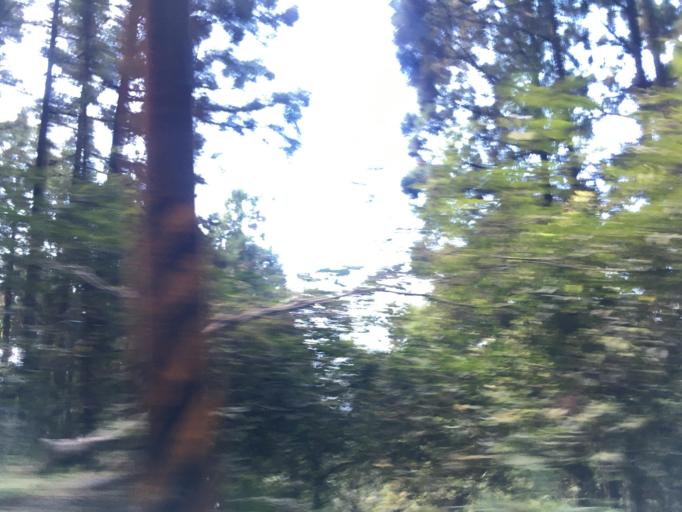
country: TW
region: Taiwan
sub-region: Yilan
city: Yilan
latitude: 24.6167
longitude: 121.4823
